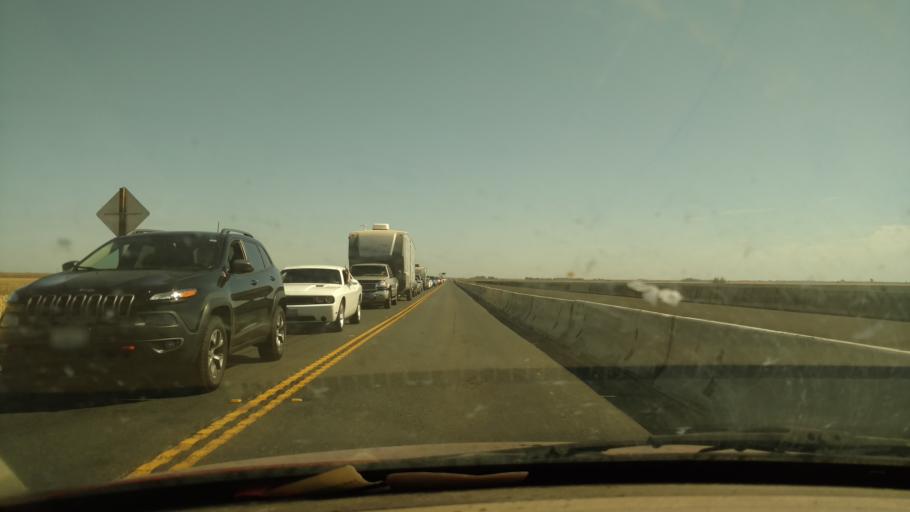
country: US
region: California
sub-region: Solano County
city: Rio Vista
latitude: 38.1228
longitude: -121.5729
